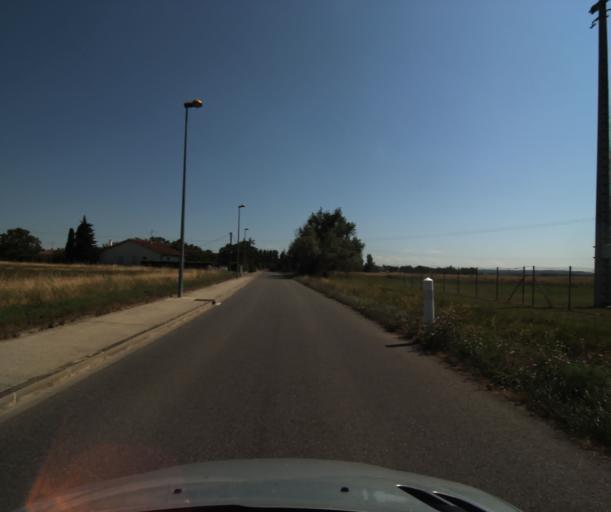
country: FR
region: Midi-Pyrenees
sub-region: Departement de la Haute-Garonne
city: Roquettes
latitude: 43.4752
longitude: 1.3803
